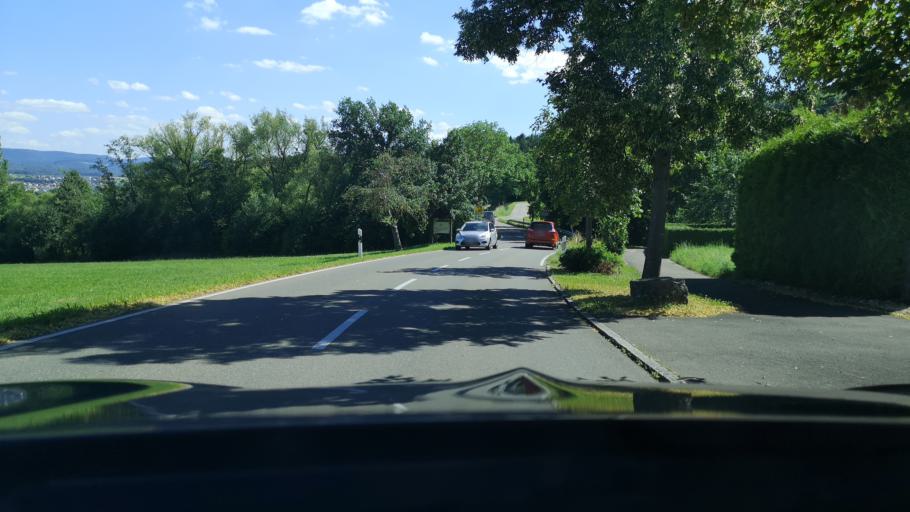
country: DE
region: Baden-Wuerttemberg
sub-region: Regierungsbezirk Stuttgart
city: Altenriet
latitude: 48.5873
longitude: 9.2190
